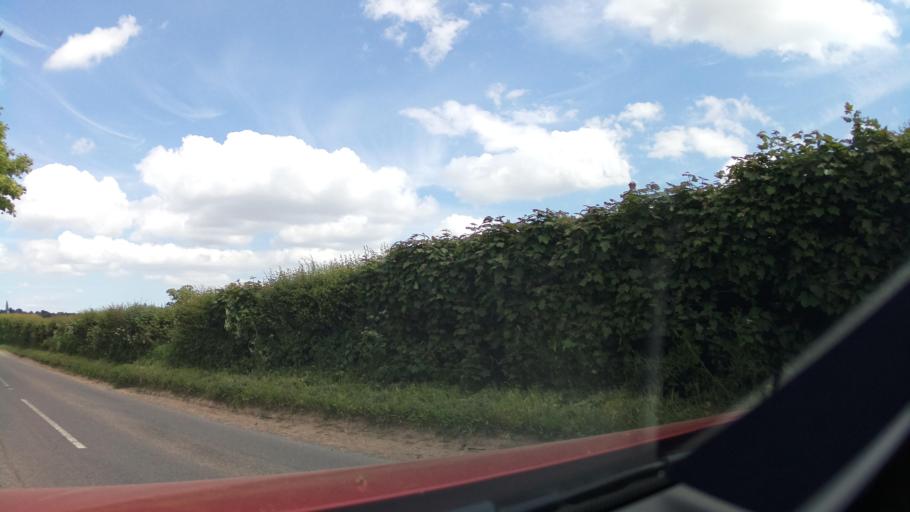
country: GB
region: England
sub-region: Herefordshire
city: Pencoyd
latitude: 51.9107
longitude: -2.6948
